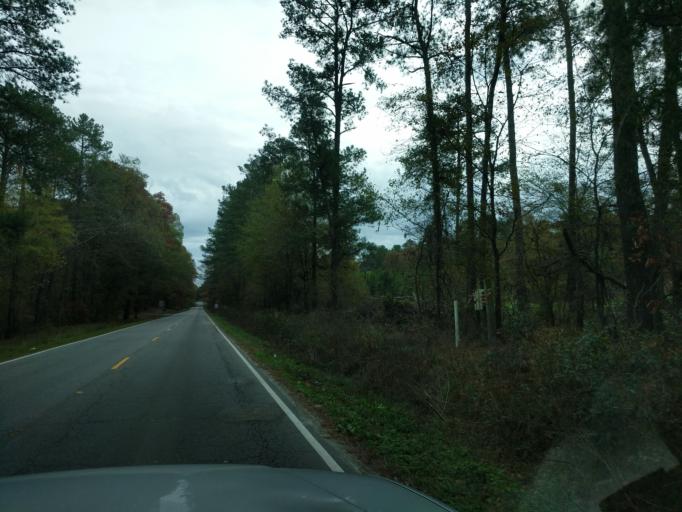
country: US
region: South Carolina
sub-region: Lexington County
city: Batesburg
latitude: 33.9542
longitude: -81.6358
